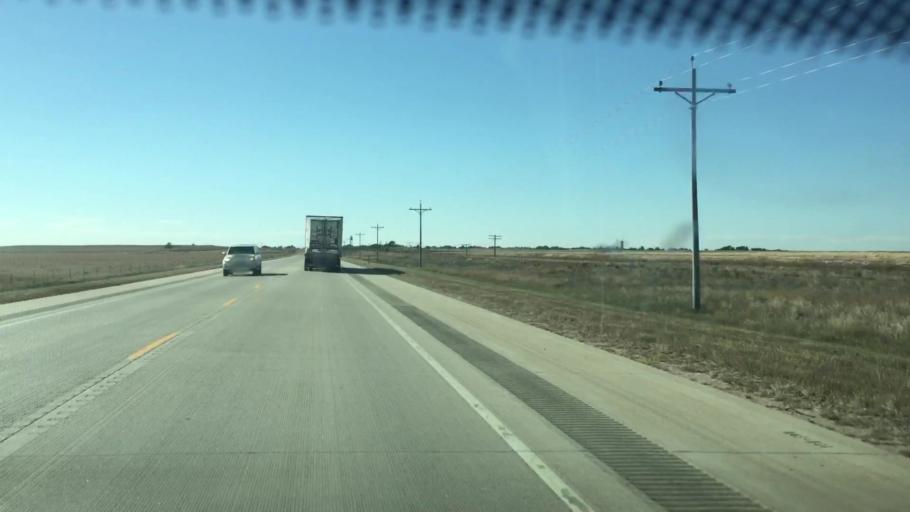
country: US
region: Colorado
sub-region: Kiowa County
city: Eads
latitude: 38.4754
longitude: -102.7539
